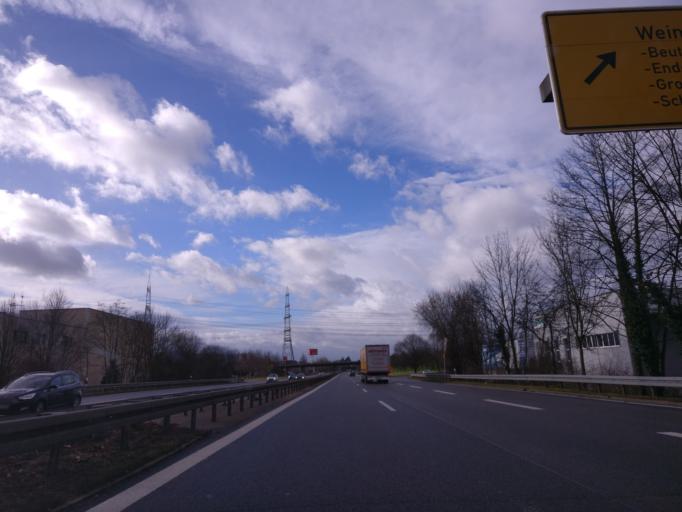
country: DE
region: Baden-Wuerttemberg
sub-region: Regierungsbezirk Stuttgart
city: Weinstadt-Endersbach
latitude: 48.8152
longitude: 9.3839
